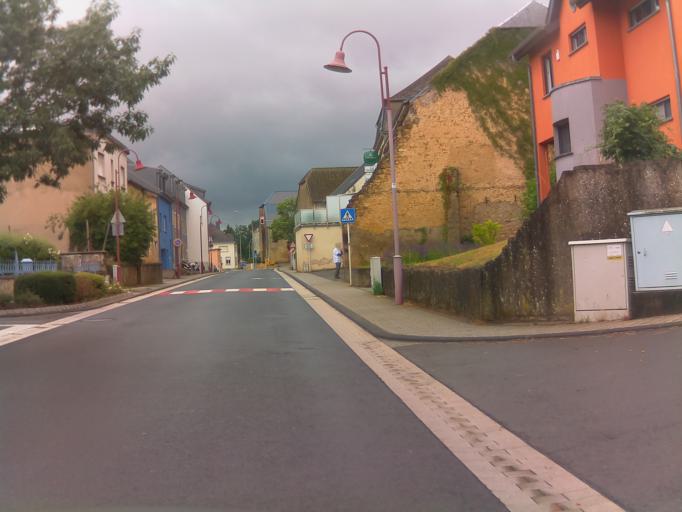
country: LU
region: Grevenmacher
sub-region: Canton de Remich
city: Dalheim
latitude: 49.5331
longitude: 6.2494
